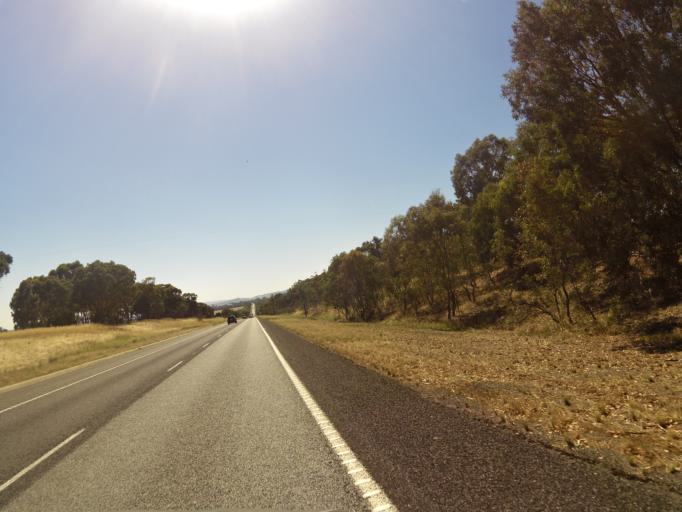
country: AU
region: Victoria
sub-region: Greater Shepparton
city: Shepparton
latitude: -36.8321
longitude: 145.3902
